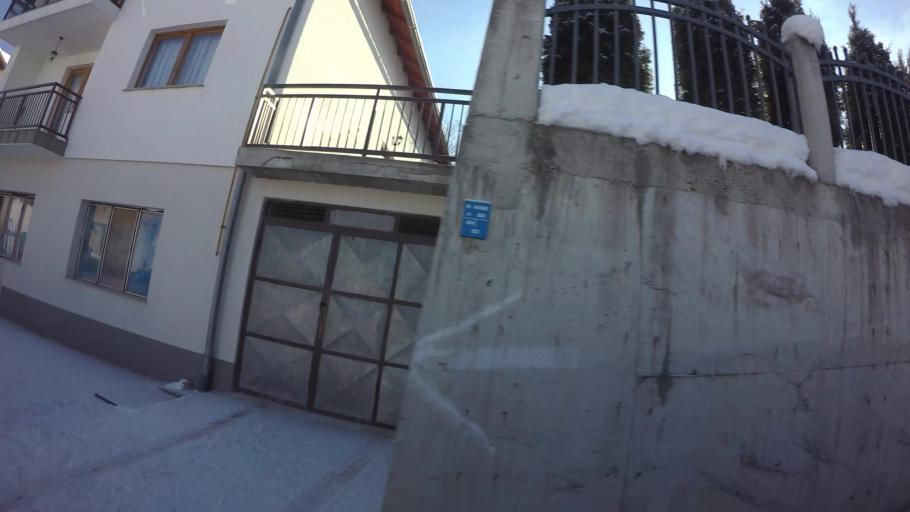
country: BA
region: Federation of Bosnia and Herzegovina
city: Kobilja Glava
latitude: 43.8778
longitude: 18.4229
